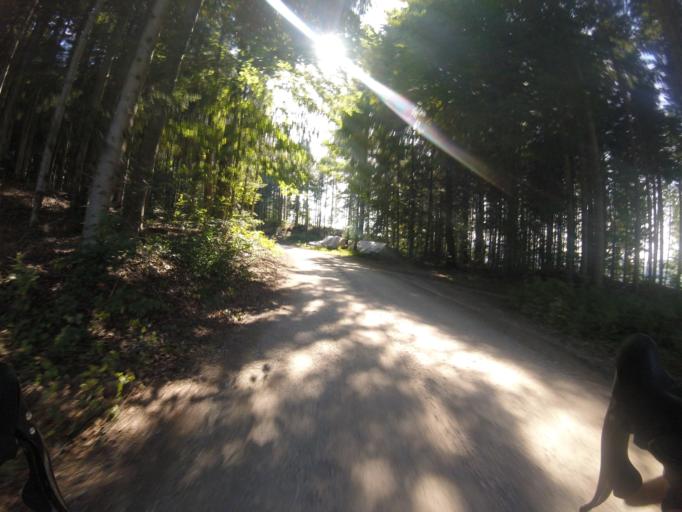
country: CH
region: Bern
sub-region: Bern-Mittelland District
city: Toffen
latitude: 46.8640
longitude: 7.5148
